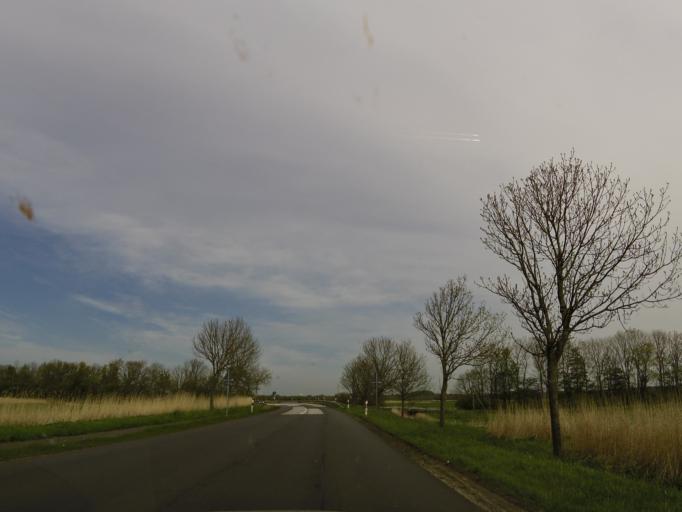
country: DE
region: Schleswig-Holstein
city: Husum
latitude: 54.4473
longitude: 9.0474
